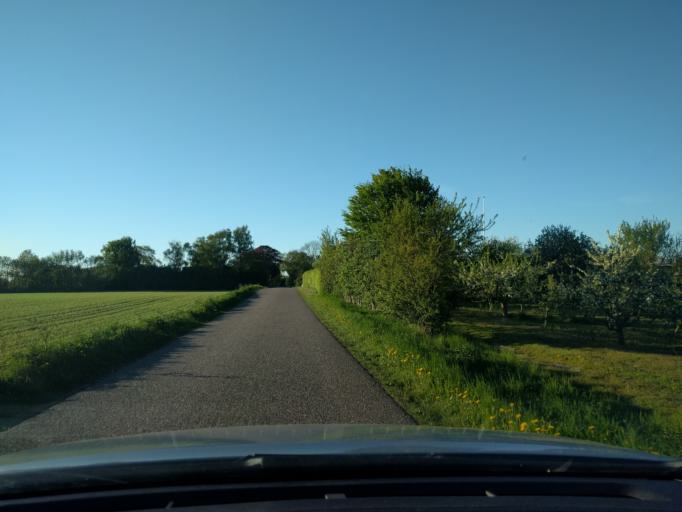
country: DK
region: South Denmark
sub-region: Nyborg Kommune
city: Ullerslev
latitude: 55.3946
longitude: 10.6491
